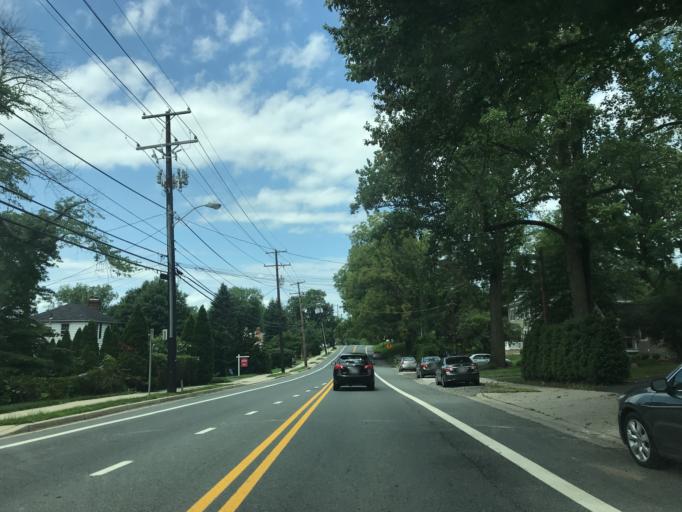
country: US
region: Maryland
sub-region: Montgomery County
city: Kensington
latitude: 39.0280
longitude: -77.0801
